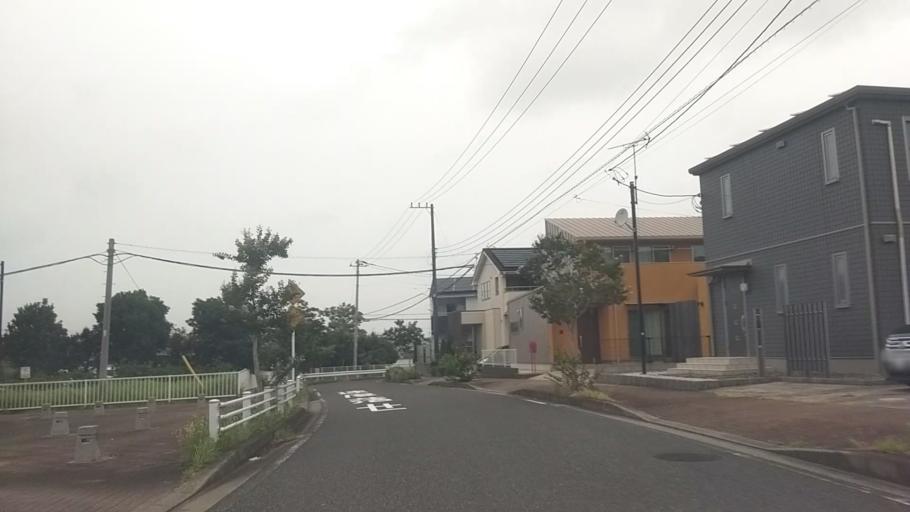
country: JP
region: Chiba
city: Kisarazu
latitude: 35.3852
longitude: 139.9657
